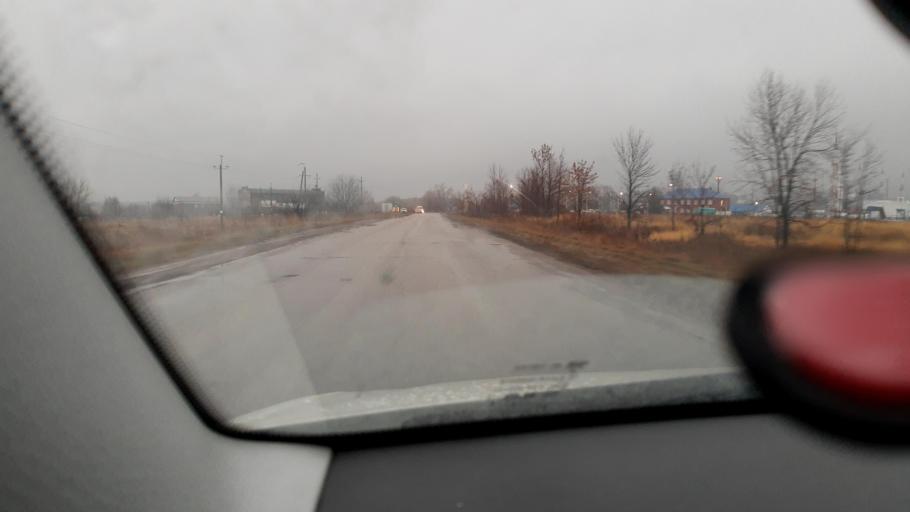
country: RU
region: Bashkortostan
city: Blagoveshchensk
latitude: 54.8964
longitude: 56.1525
